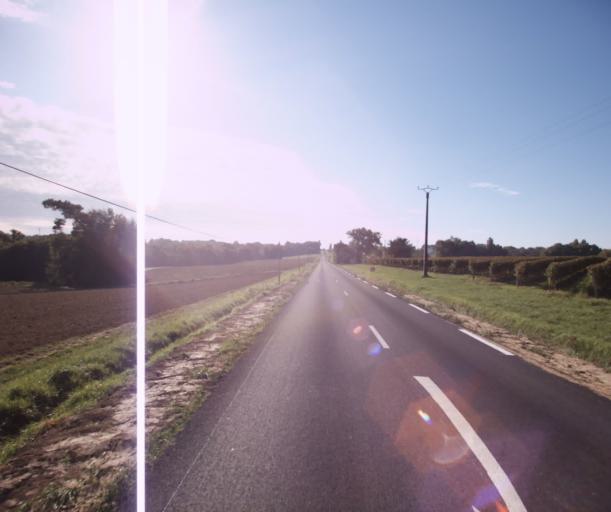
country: FR
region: Midi-Pyrenees
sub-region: Departement du Gers
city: Cazaubon
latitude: 43.8988
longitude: -0.0133
